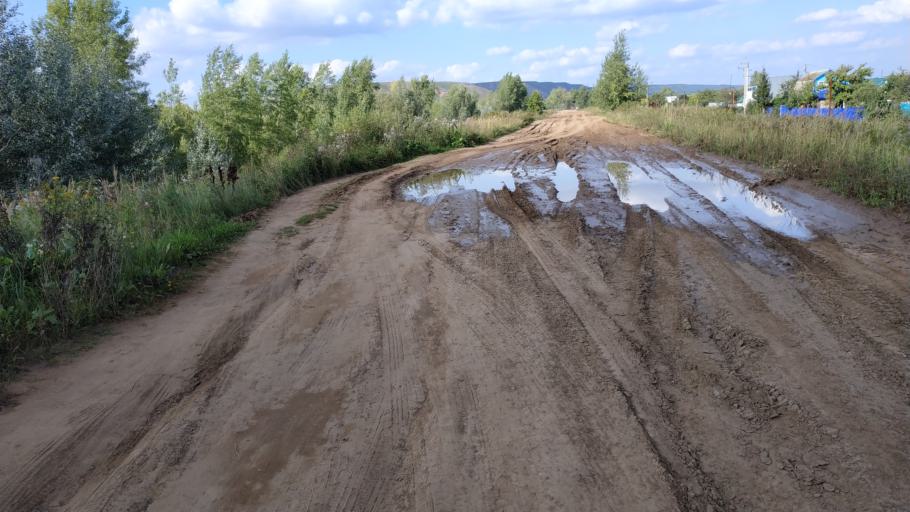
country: RU
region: Tatarstan
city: Nizhnekamsk
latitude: 55.6830
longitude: 51.7306
